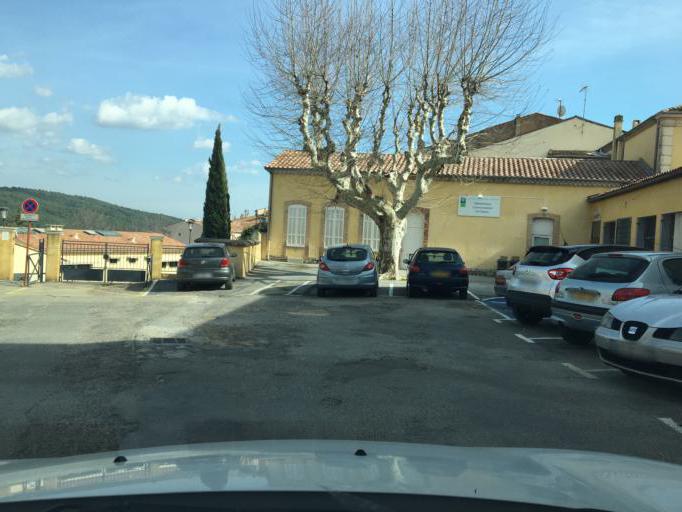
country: FR
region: Provence-Alpes-Cote d'Azur
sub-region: Departement du Var
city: Flayosc
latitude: 43.5347
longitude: 6.3952
